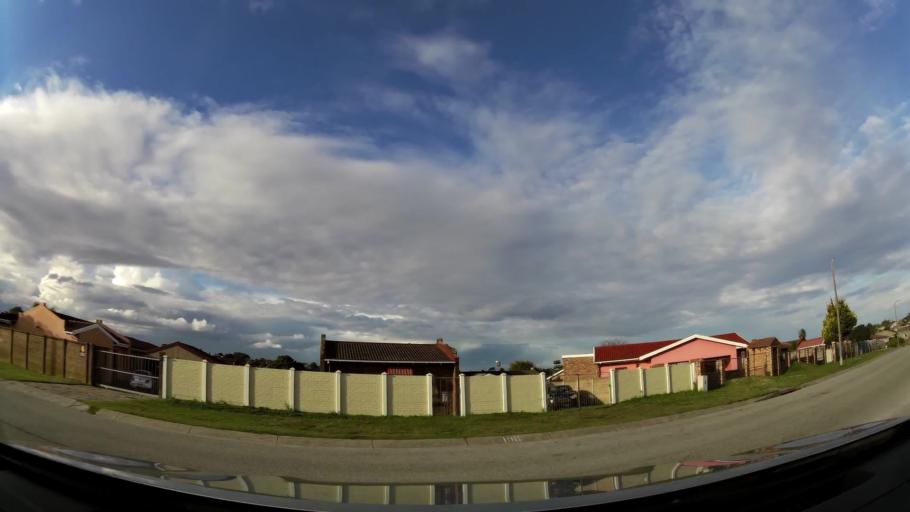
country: ZA
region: Eastern Cape
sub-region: Nelson Mandela Bay Metropolitan Municipality
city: Port Elizabeth
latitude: -33.9646
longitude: 25.4764
